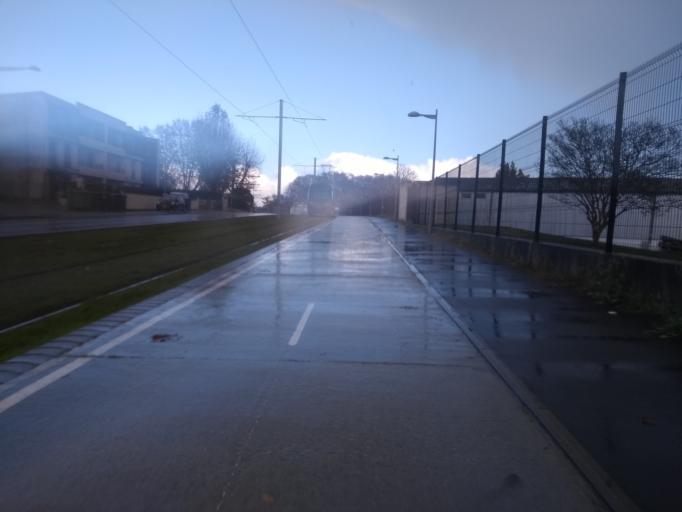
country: FR
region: Aquitaine
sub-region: Departement de la Gironde
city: Begles
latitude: 44.7907
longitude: -0.5630
